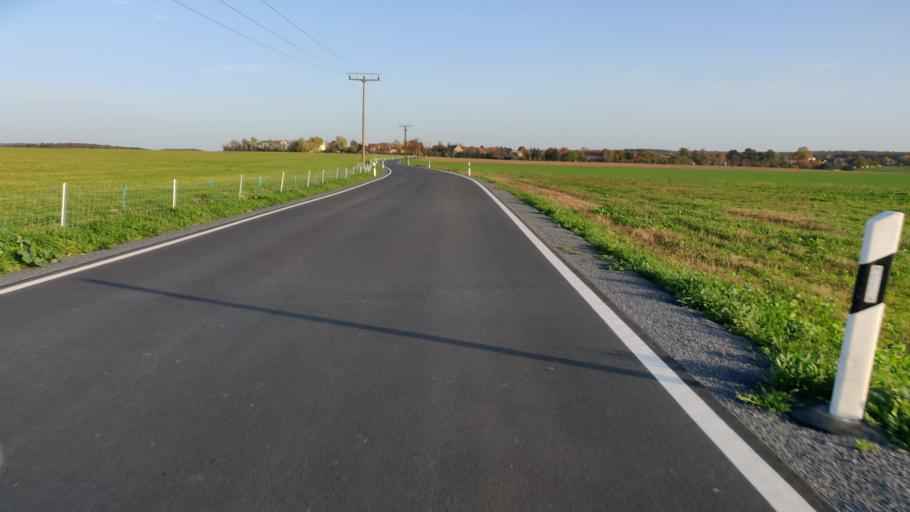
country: DE
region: Brandenburg
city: Grossthiemig
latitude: 51.3501
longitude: 13.6443
